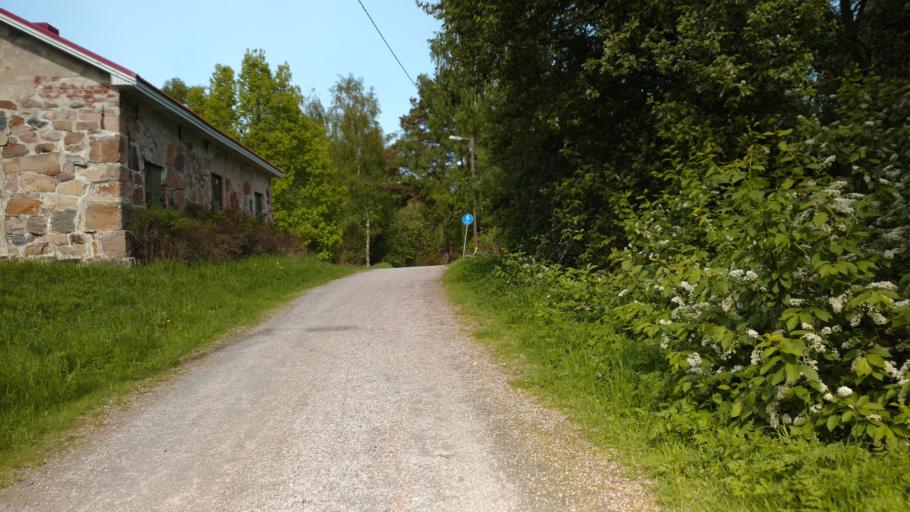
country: FI
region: Varsinais-Suomi
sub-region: Salo
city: Halikko
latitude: 60.3898
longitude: 23.0998
